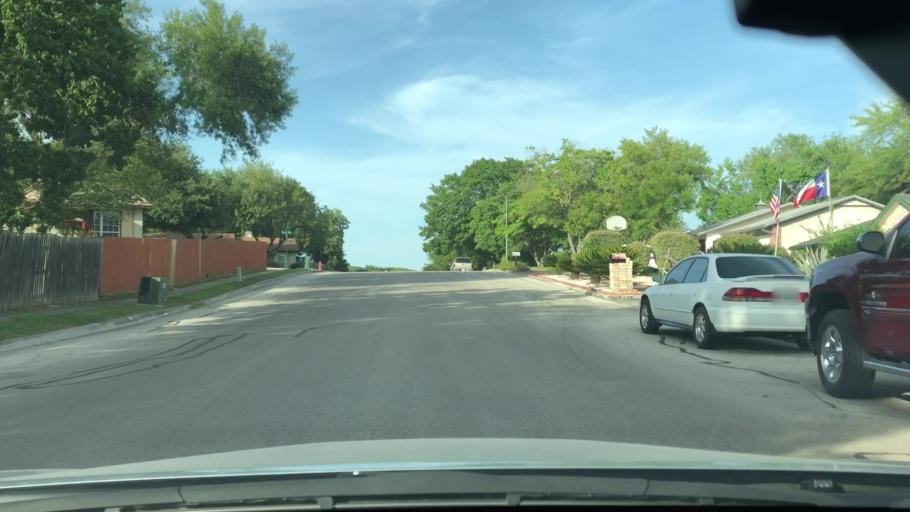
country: US
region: Texas
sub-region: Bexar County
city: Converse
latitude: 29.5350
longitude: -98.3198
